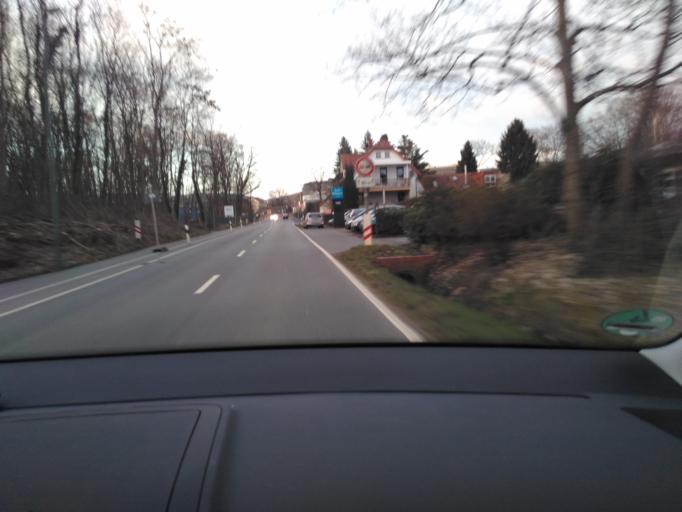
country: DE
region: North Rhine-Westphalia
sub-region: Regierungsbezirk Detmold
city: Bielefeld
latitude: 51.9724
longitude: 8.5074
